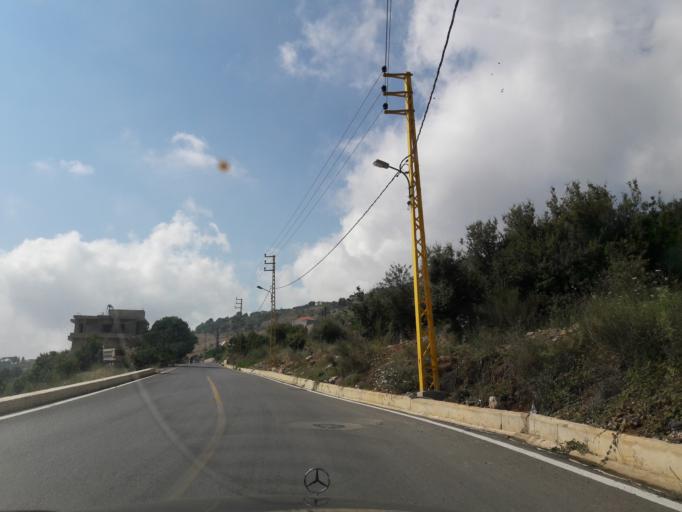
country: LB
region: Mont-Liban
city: Djounie
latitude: 33.9645
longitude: 35.7742
